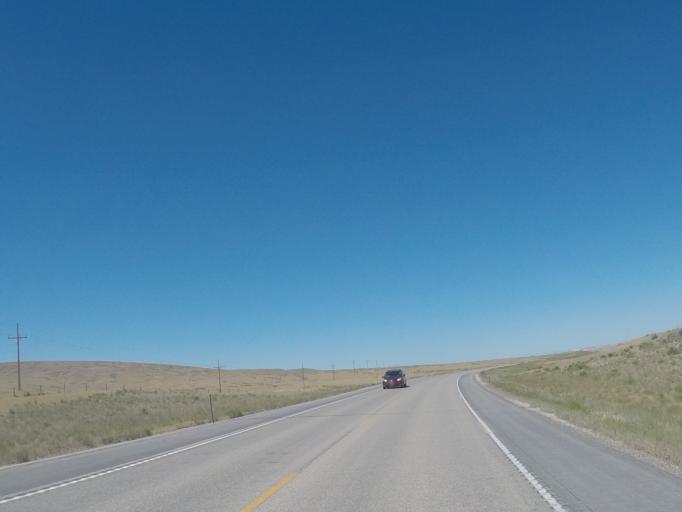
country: US
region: Wyoming
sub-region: Big Horn County
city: Greybull
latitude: 44.5174
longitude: -107.8453
